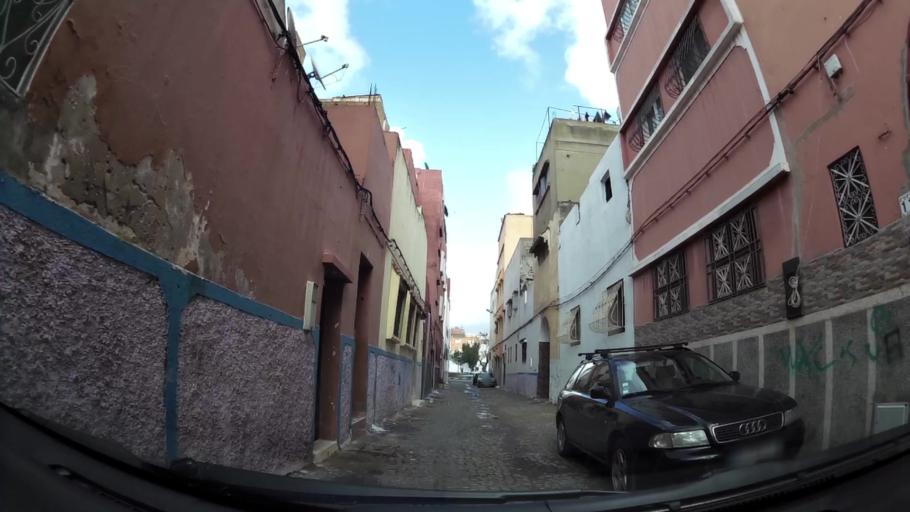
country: MA
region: Grand Casablanca
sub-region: Casablanca
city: Casablanca
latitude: 33.5514
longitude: -7.5982
